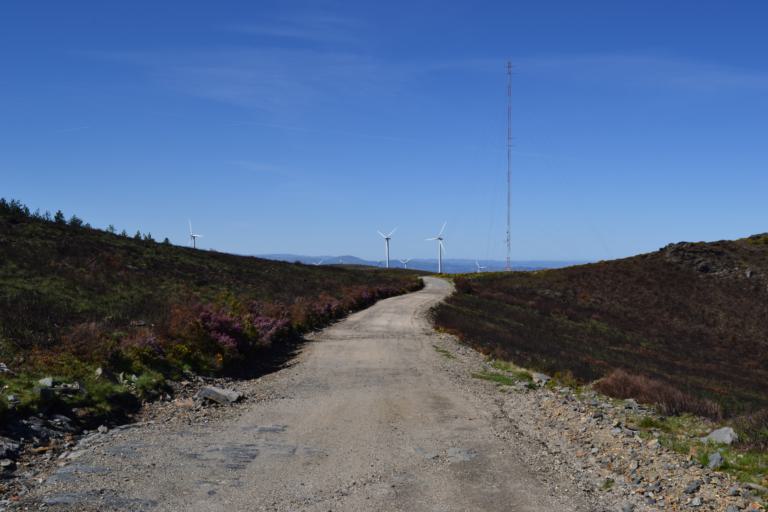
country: PT
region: Vila Real
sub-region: Mesao Frio
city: Mesao Frio
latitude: 41.2451
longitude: -7.8978
